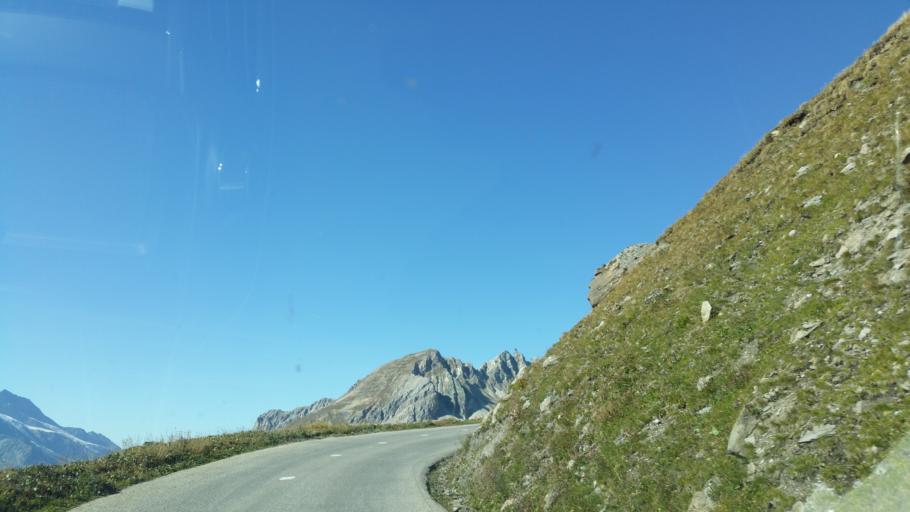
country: FR
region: Rhone-Alpes
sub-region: Departement de la Savoie
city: Val-d'Isere
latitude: 45.4349
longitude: 7.0065
